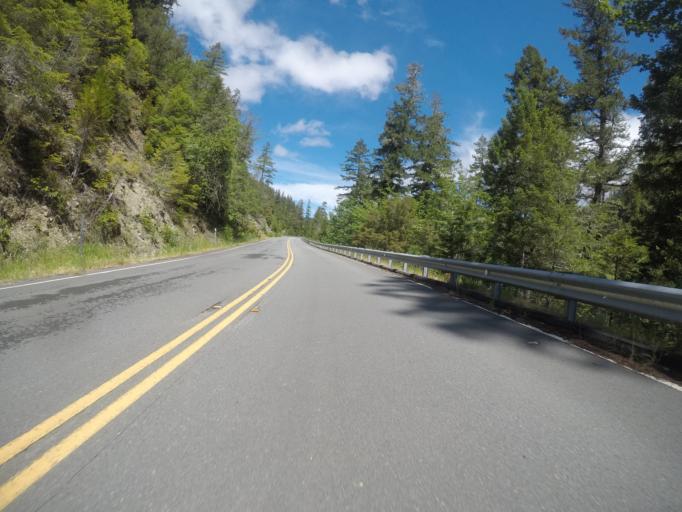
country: US
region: California
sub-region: Del Norte County
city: Bertsch-Oceanview
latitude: 41.7178
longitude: -123.9452
